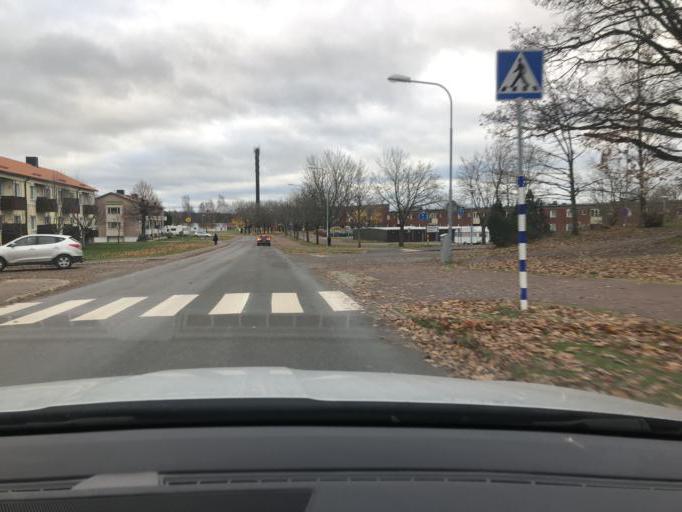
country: SE
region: Uppsala
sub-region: Tierps Kommun
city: Tierp
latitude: 60.3414
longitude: 17.5129
